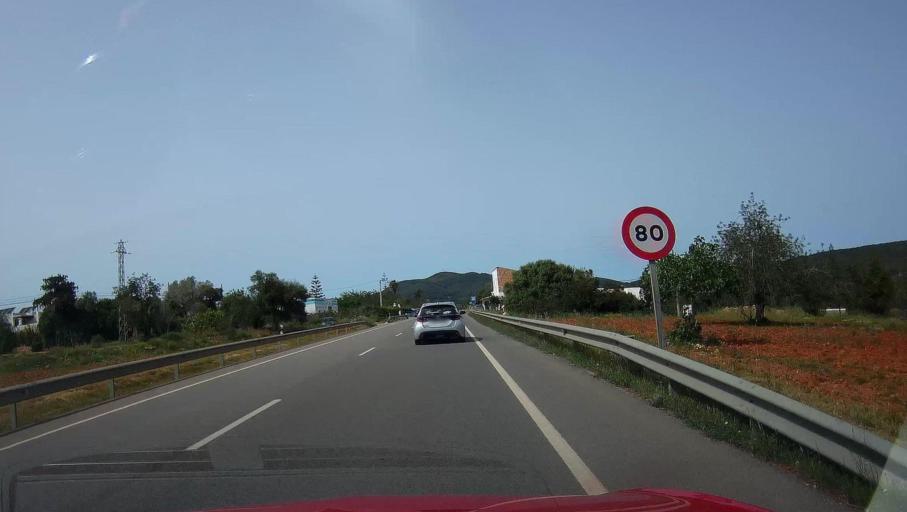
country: ES
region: Balearic Islands
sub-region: Illes Balears
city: Sant Joan de Labritja
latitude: 39.0441
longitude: 1.4918
